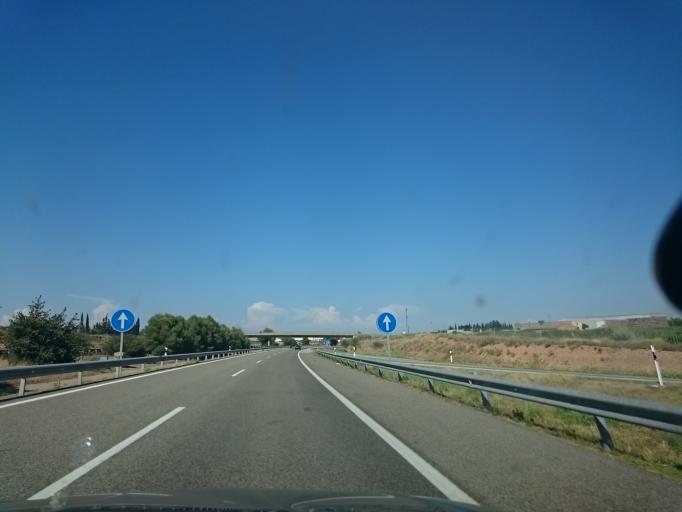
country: ES
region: Catalonia
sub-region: Provincia de Lleida
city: Soses
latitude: 41.5372
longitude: 0.4772
